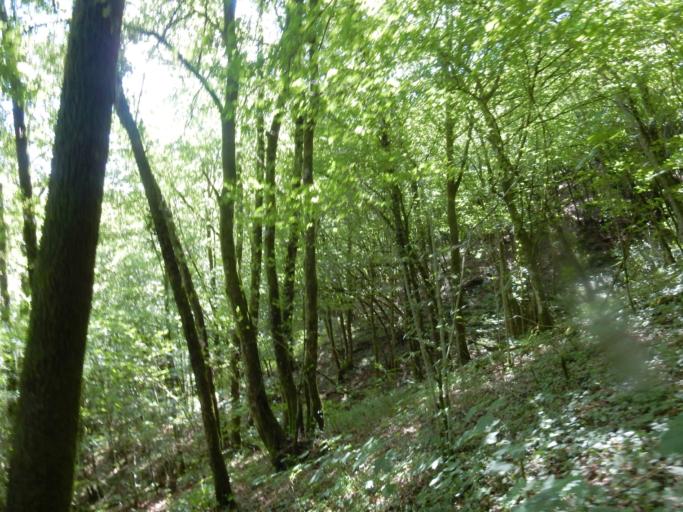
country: LU
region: Diekirch
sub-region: Canton de Diekirch
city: Bourscheid
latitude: 49.9414
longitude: 6.0631
